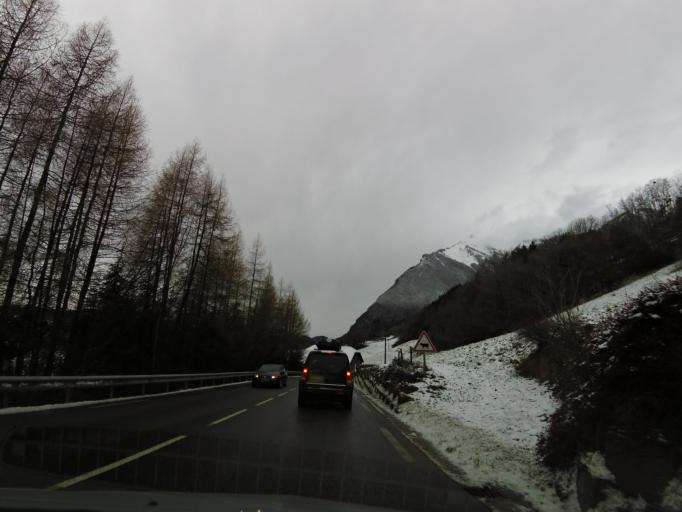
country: FR
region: Rhone-Alpes
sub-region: Departement de la Haute-Savoie
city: Taninges
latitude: 46.1096
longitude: 6.6137
